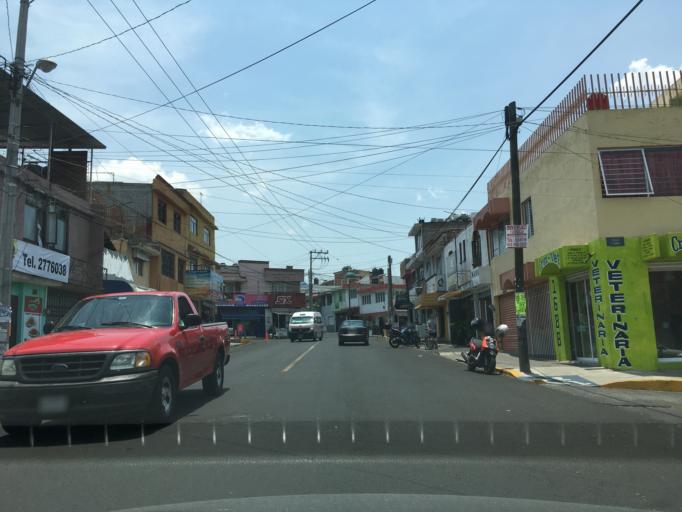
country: MX
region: Michoacan
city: Morelia
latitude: 19.7018
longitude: -101.1639
